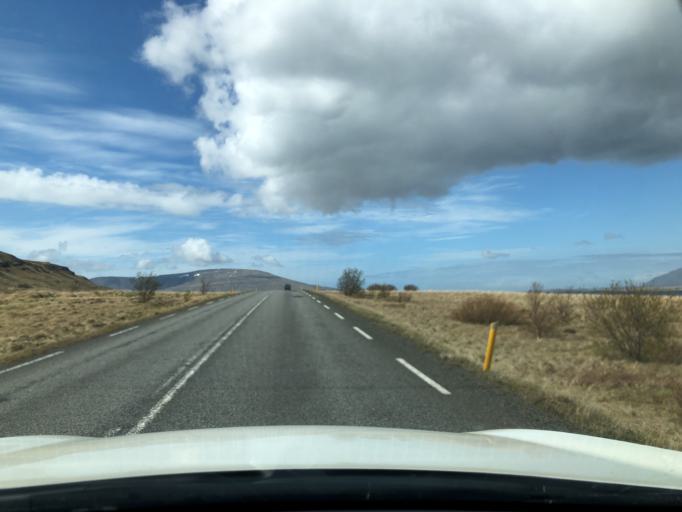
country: IS
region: Capital Region
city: Mosfellsbaer
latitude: 64.3312
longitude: -21.6812
